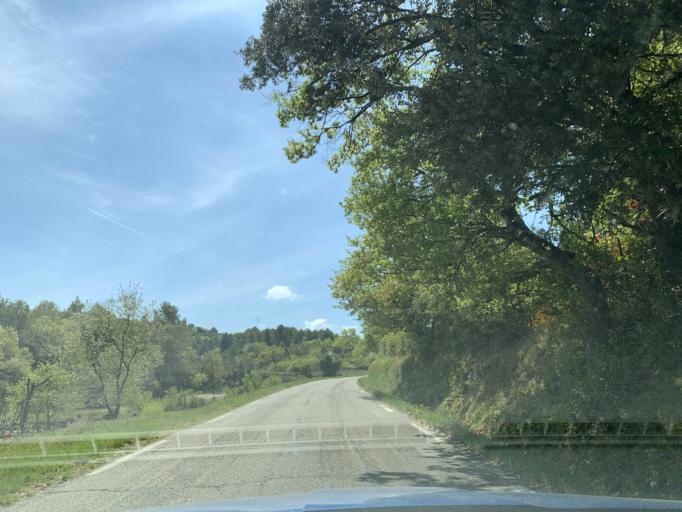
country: FR
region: Provence-Alpes-Cote d'Azur
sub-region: Departement du Vaucluse
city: Saint-Didier
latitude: 43.9982
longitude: 5.1070
